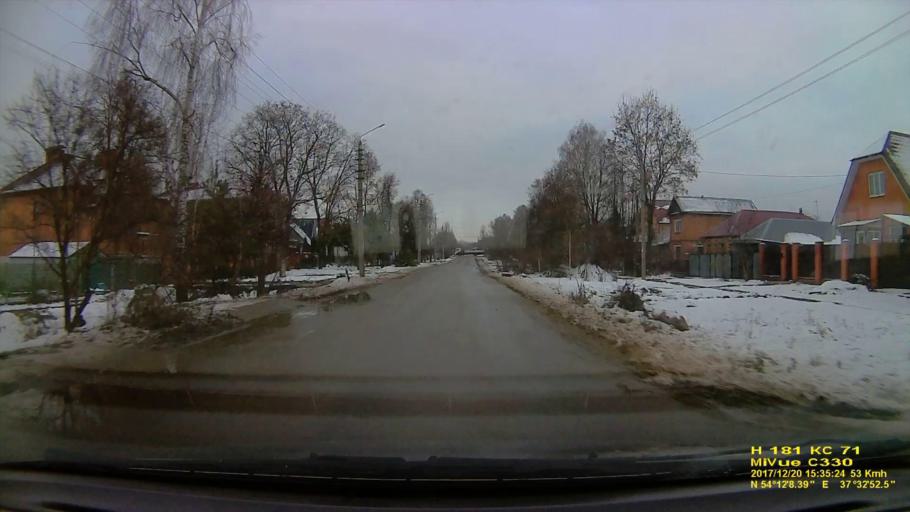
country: RU
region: Tula
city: Tula
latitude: 54.2022
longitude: 37.5481
